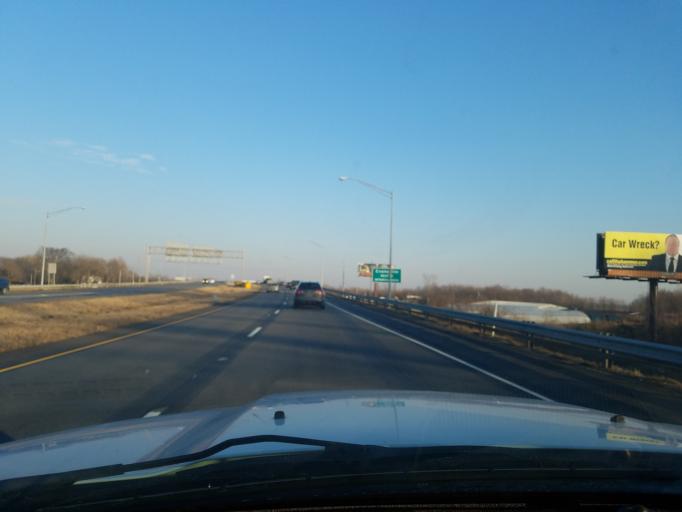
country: US
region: Indiana
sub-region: Vanderburgh County
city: Evansville
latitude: 37.9359
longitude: -87.5335
